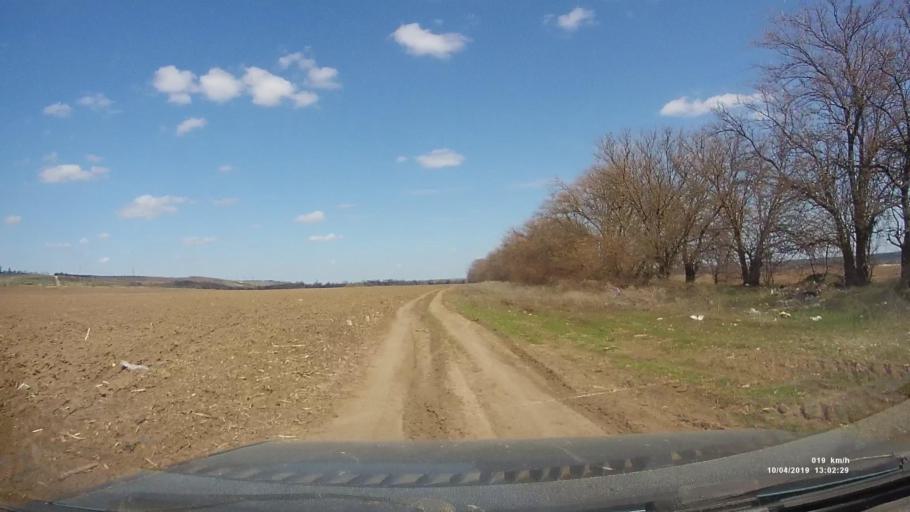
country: RU
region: Rostov
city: Masalovka
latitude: 48.3814
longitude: 40.2310
